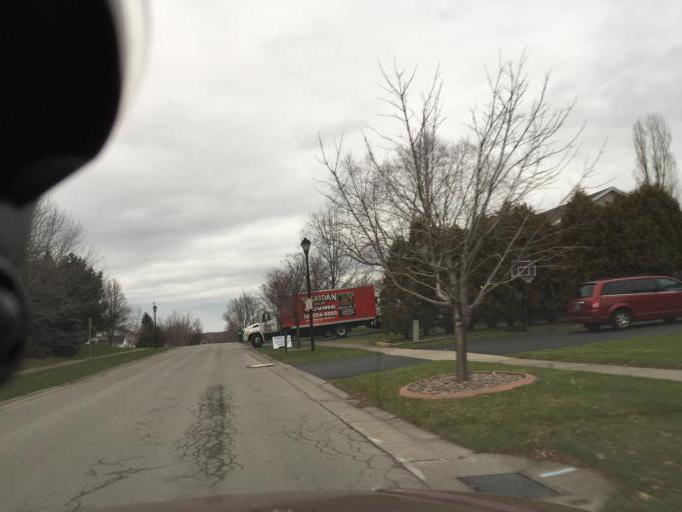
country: US
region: New York
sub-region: Monroe County
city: Greece
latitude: 43.2532
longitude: -77.6583
